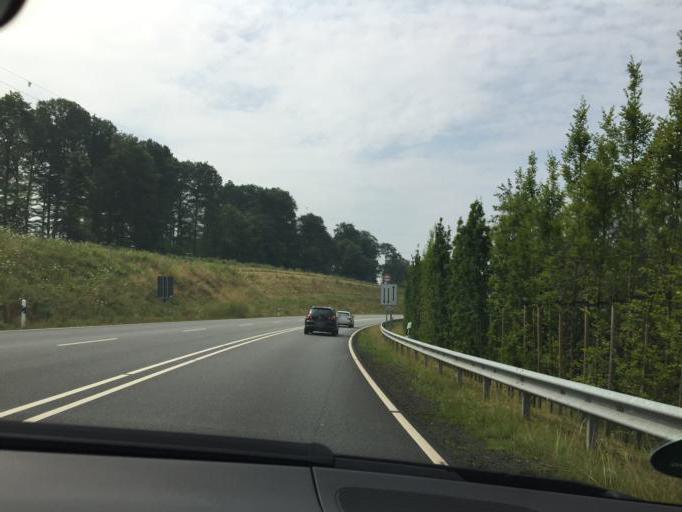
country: DE
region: Rheinland-Pfalz
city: Rengsdorf
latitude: 50.5048
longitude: 7.4810
